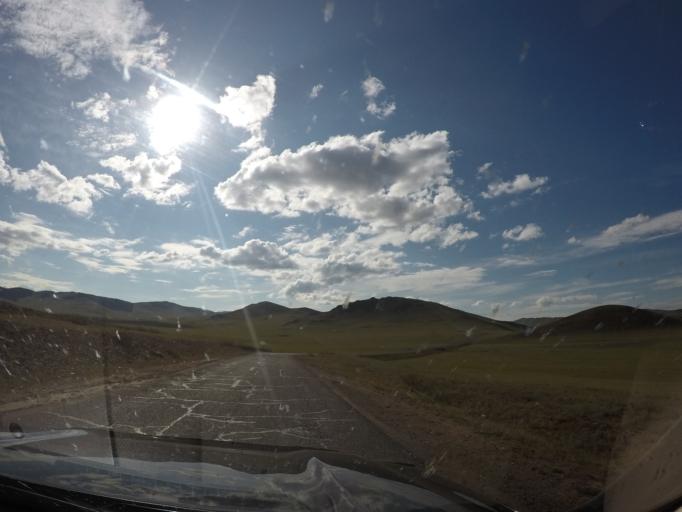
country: MN
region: Hentiy
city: Modot
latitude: 47.7521
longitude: 108.9466
